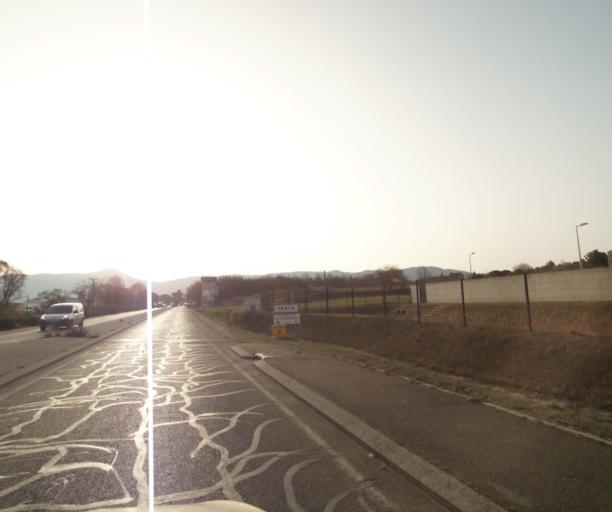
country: FR
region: Provence-Alpes-Cote d'Azur
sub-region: Departement des Bouches-du-Rhone
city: Trets
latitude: 43.4519
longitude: 5.6724
